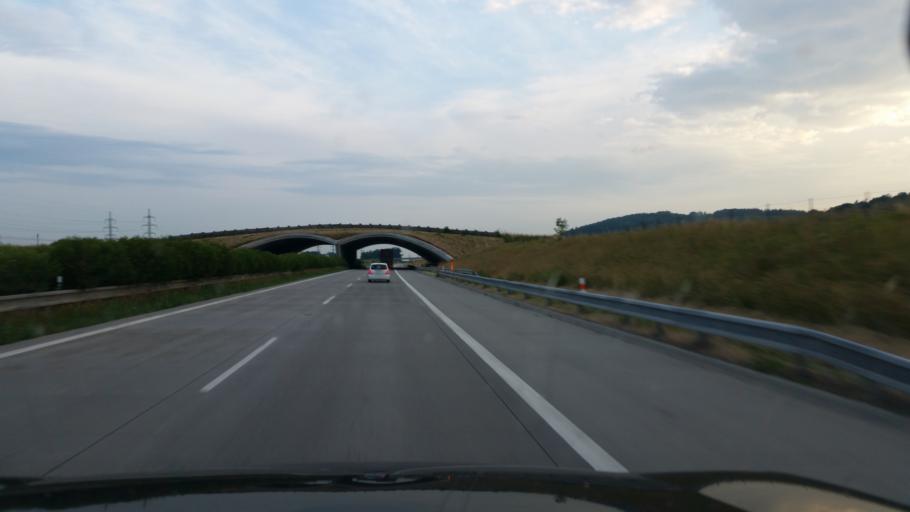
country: CZ
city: Fulnek
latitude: 49.6713
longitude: 17.9240
